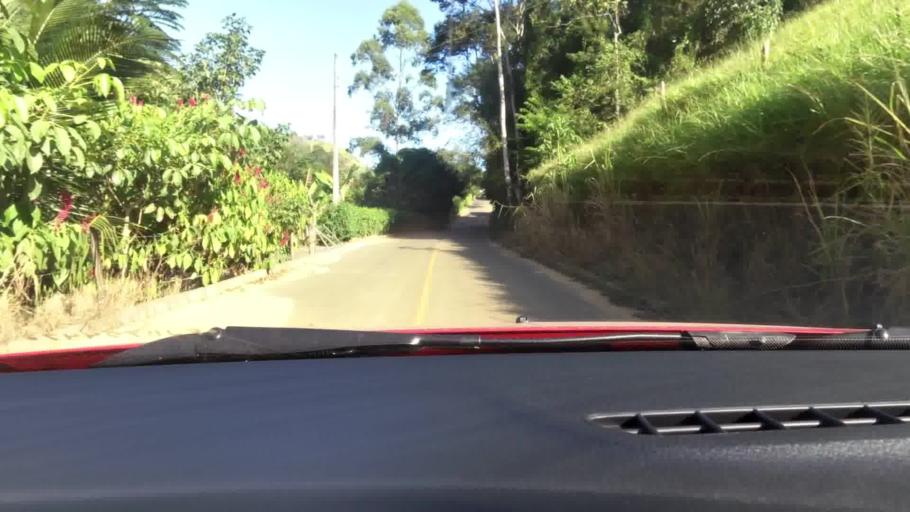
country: BR
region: Espirito Santo
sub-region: Guarapari
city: Guarapari
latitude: -20.5455
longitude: -40.5577
